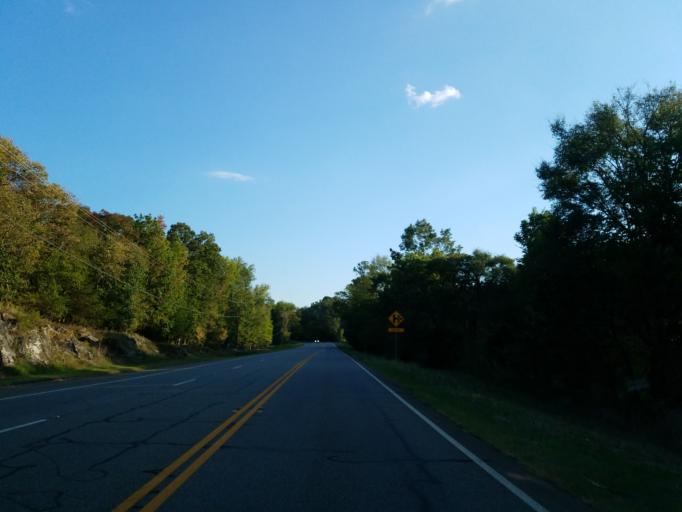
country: US
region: Georgia
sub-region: Bartow County
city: Rydal
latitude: 34.5461
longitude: -84.7073
